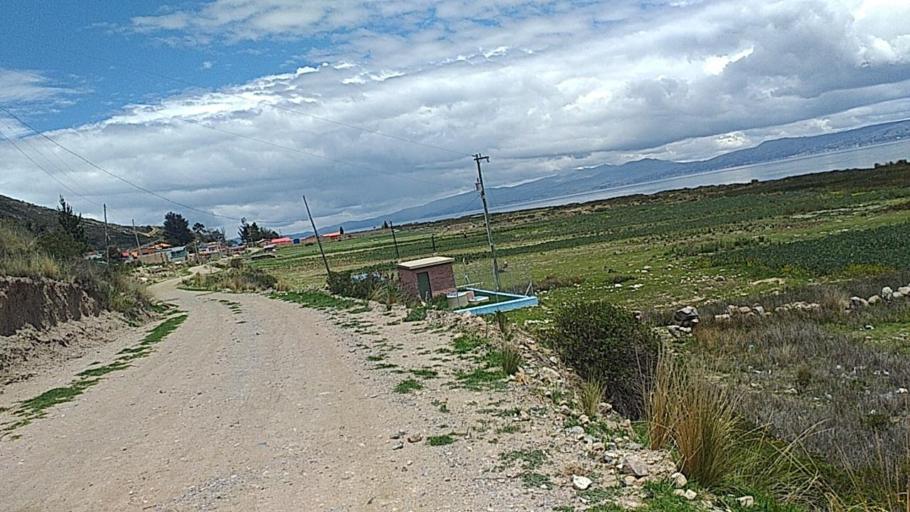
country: BO
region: La Paz
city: Huatajata
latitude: -16.3150
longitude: -68.6736
